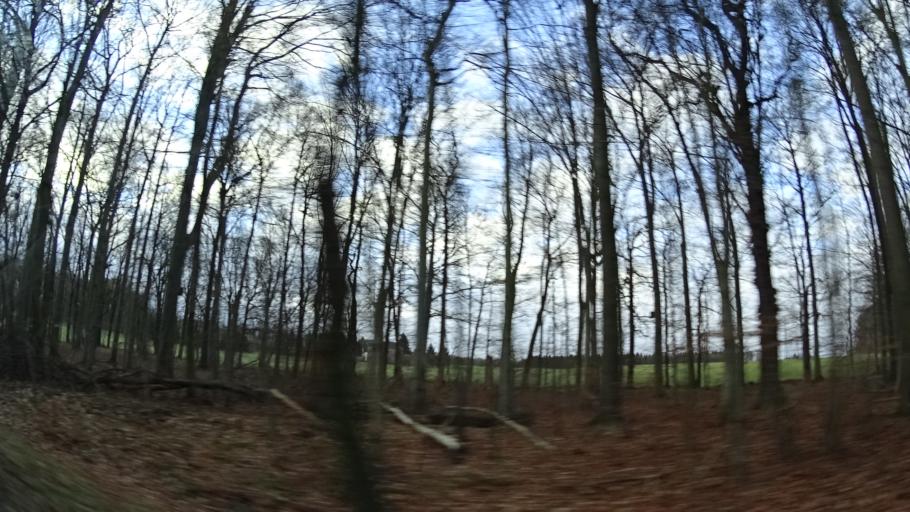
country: DE
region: Thuringia
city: Auma
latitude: 50.6780
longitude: 11.9230
